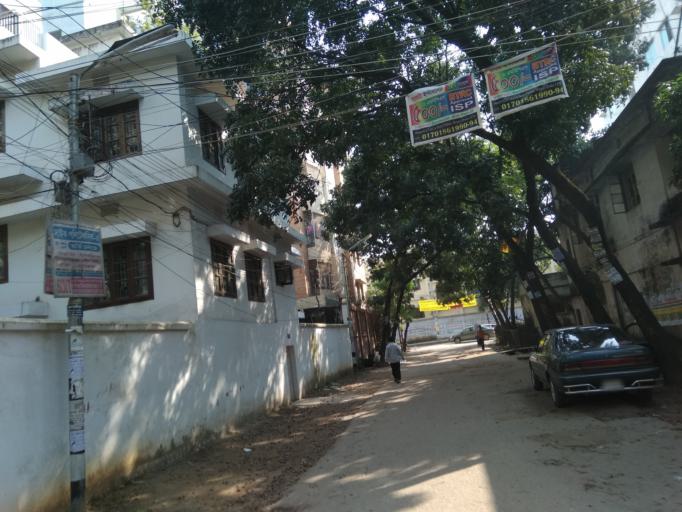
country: BD
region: Dhaka
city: Tungi
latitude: 23.8268
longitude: 90.3616
